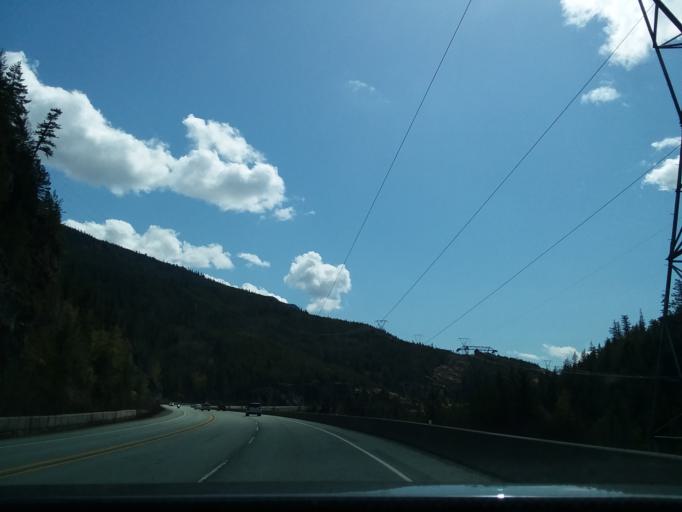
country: CA
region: British Columbia
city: Whistler
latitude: 49.9339
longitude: -123.1658
